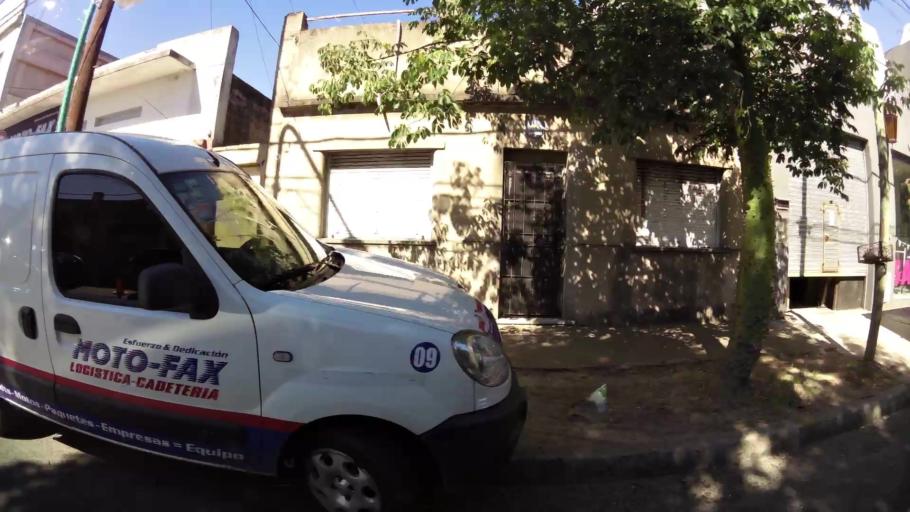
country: AR
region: Buenos Aires
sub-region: Partido de General San Martin
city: General San Martin
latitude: -34.5464
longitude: -58.5028
